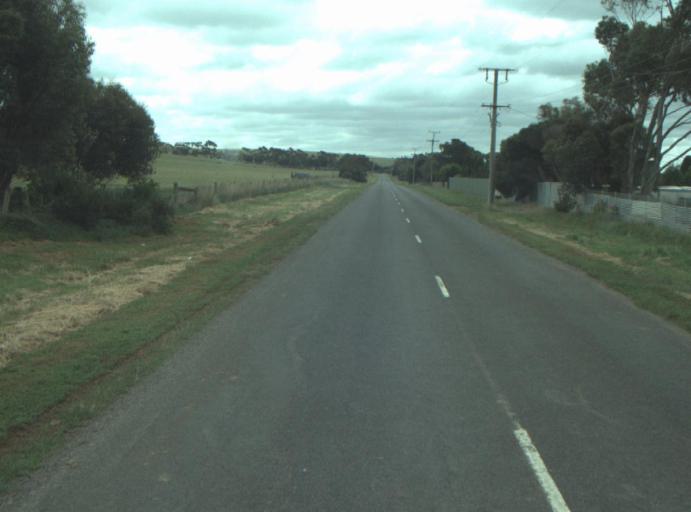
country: AU
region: Victoria
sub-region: Greater Geelong
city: Bell Post Hill
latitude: -38.0538
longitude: 144.3425
